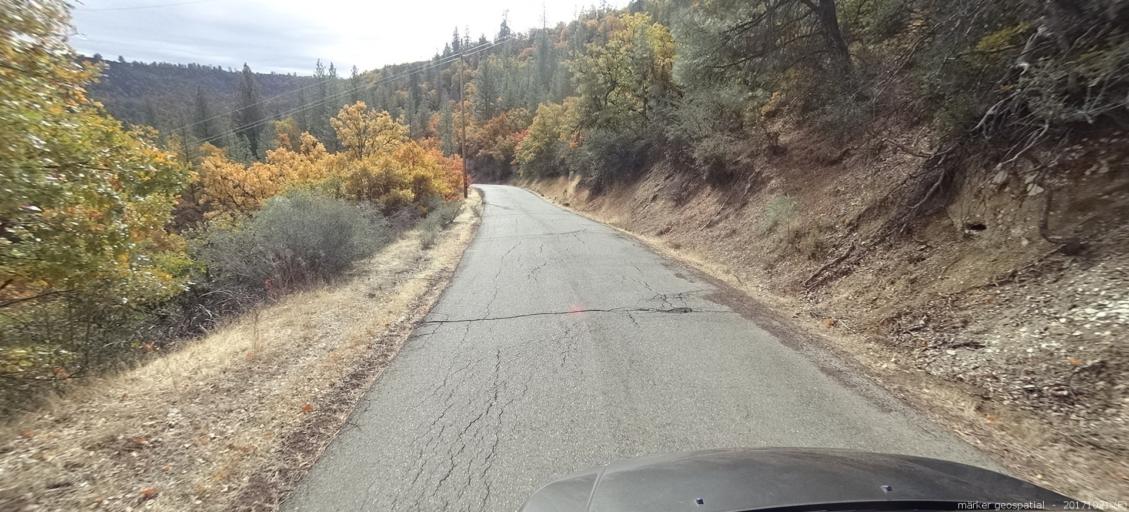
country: US
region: California
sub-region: Shasta County
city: Burney
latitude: 40.9599
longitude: -121.5538
